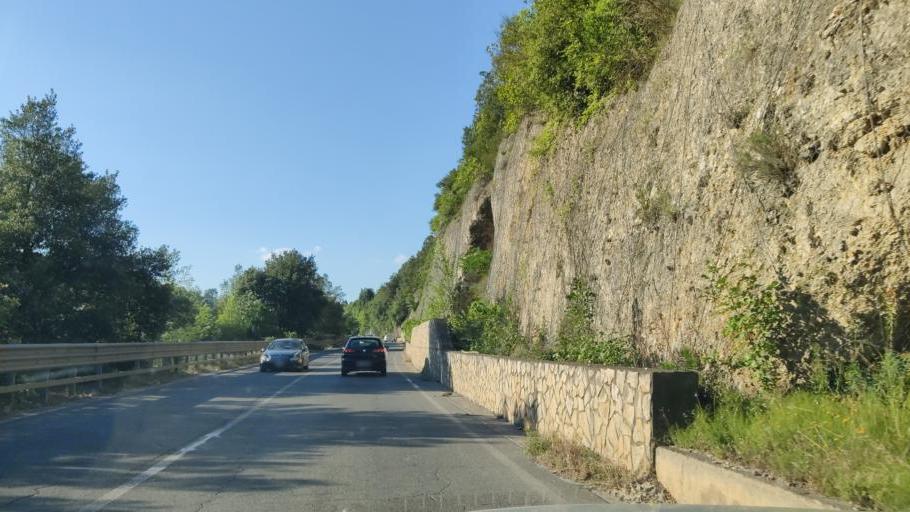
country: IT
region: Umbria
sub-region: Provincia di Terni
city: Narni
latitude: 42.5199
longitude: 12.5120
